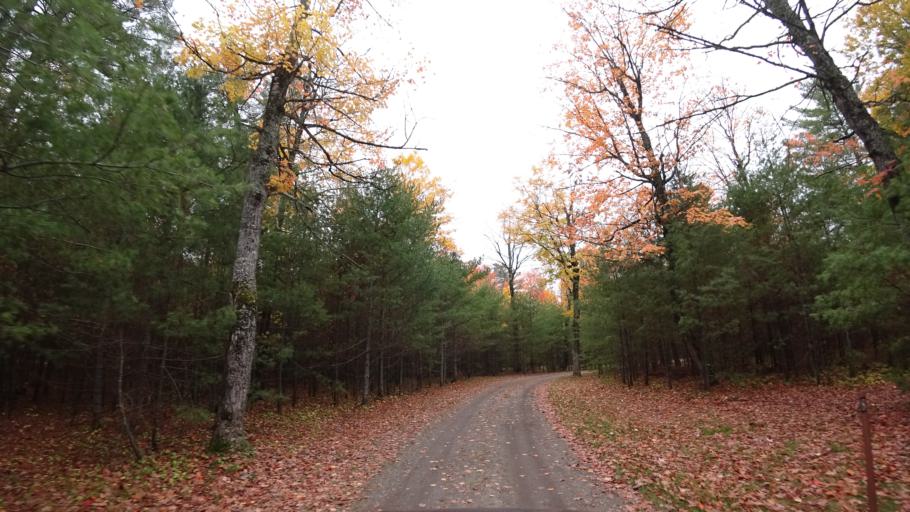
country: US
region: Michigan
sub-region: Marquette County
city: West Ishpeming
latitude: 46.5302
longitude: -88.0005
